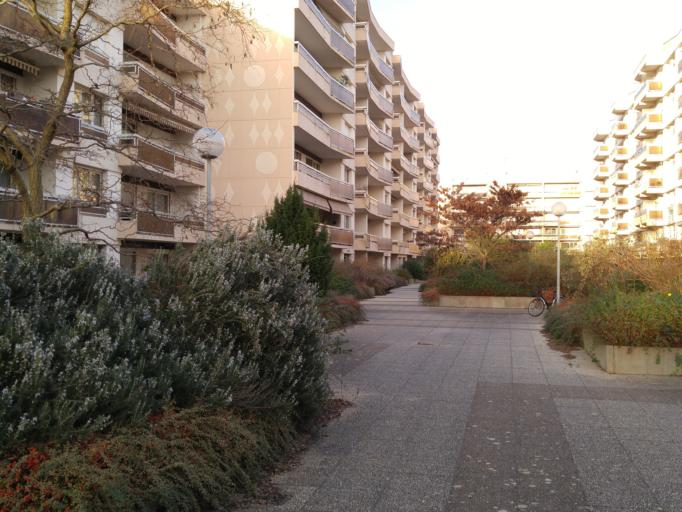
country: FR
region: Pays de la Loire
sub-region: Departement de Maine-et-Loire
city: Angers
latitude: 47.4531
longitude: -0.5563
